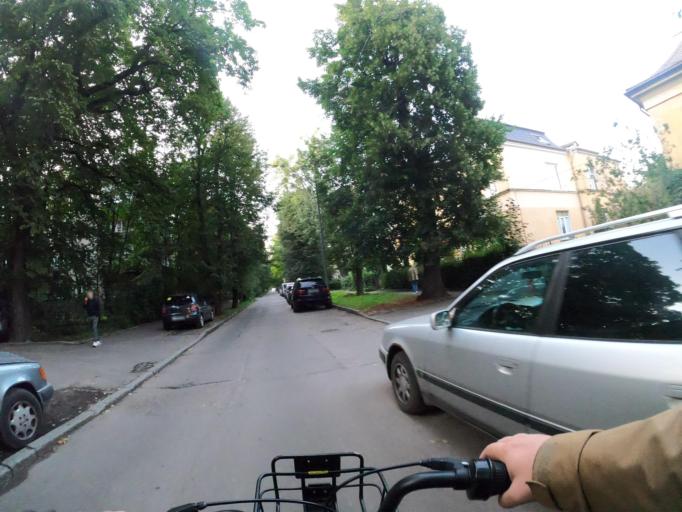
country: RU
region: Kaliningrad
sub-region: Gorod Kaliningrad
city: Kaliningrad
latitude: 54.7245
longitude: 20.4768
